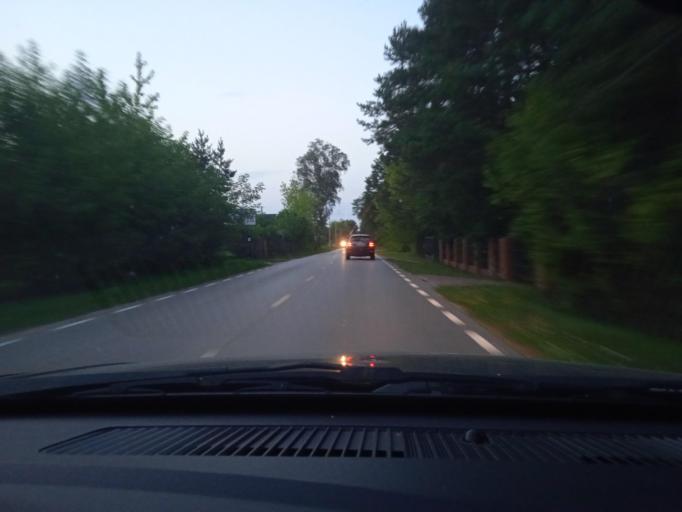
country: PL
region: Masovian Voivodeship
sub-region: Powiat nowodworski
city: Pomiechowek
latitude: 52.5147
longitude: 20.6787
